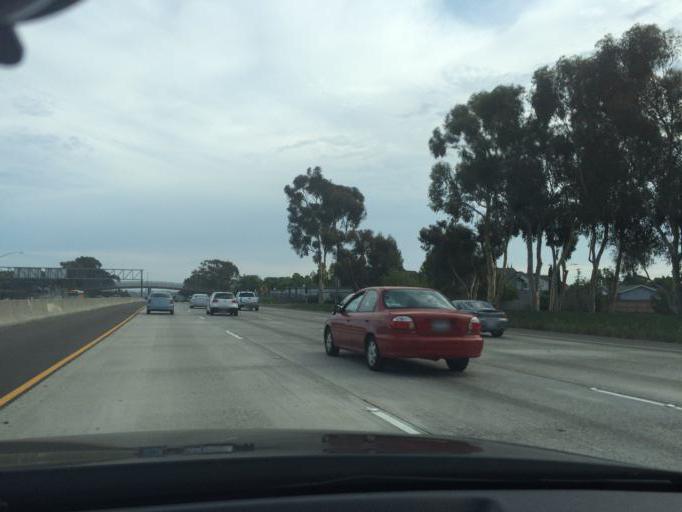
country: US
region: California
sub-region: San Diego County
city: San Diego
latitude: 32.7904
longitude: -117.1596
